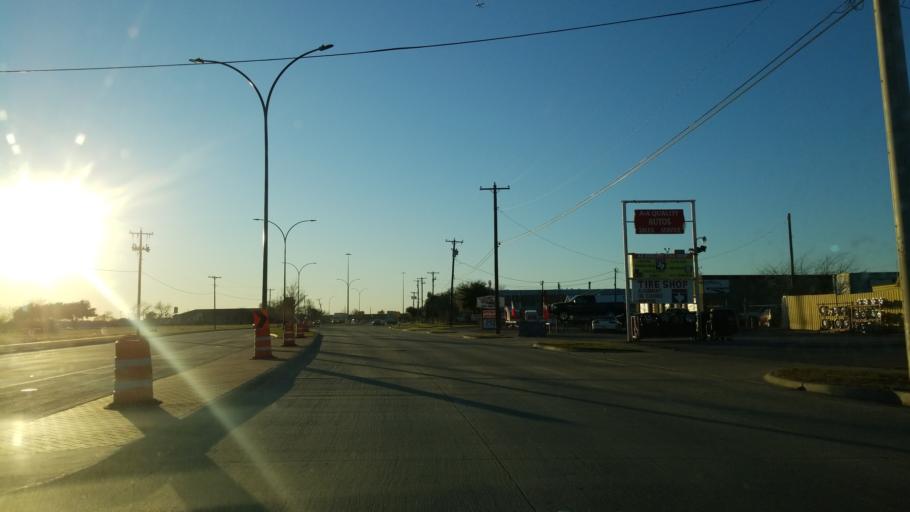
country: US
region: Texas
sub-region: Tarrant County
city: Arlington
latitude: 32.7366
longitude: -97.0566
